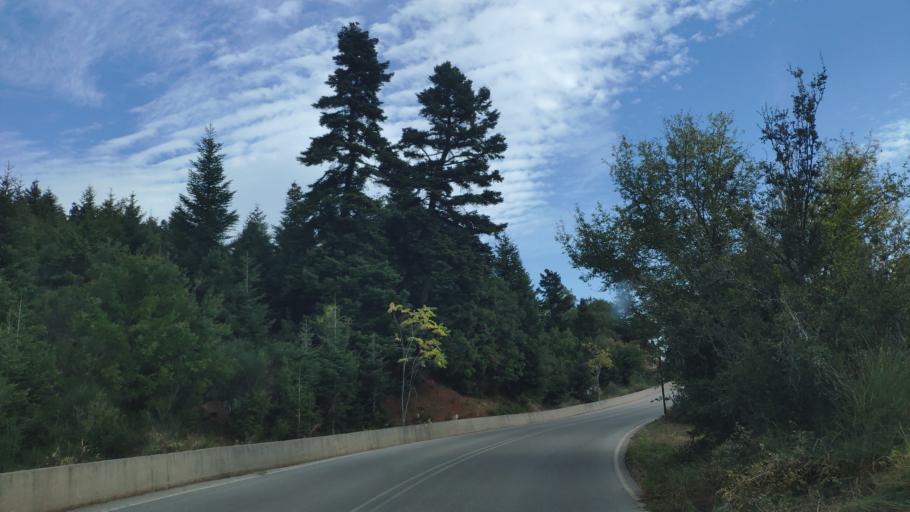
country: GR
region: Central Greece
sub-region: Nomos Fokidos
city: Amfissa
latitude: 38.6399
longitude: 22.3823
